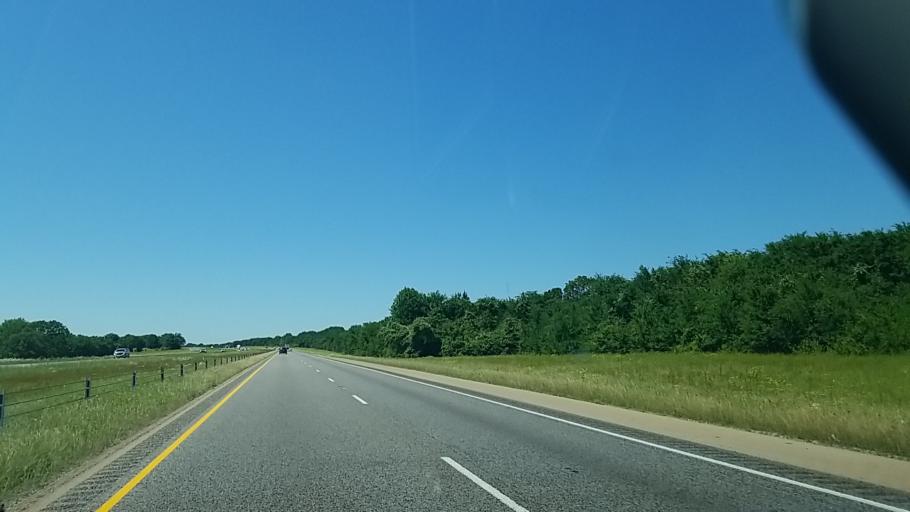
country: US
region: Texas
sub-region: Freestone County
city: Fairfield
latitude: 31.6825
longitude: -96.1651
